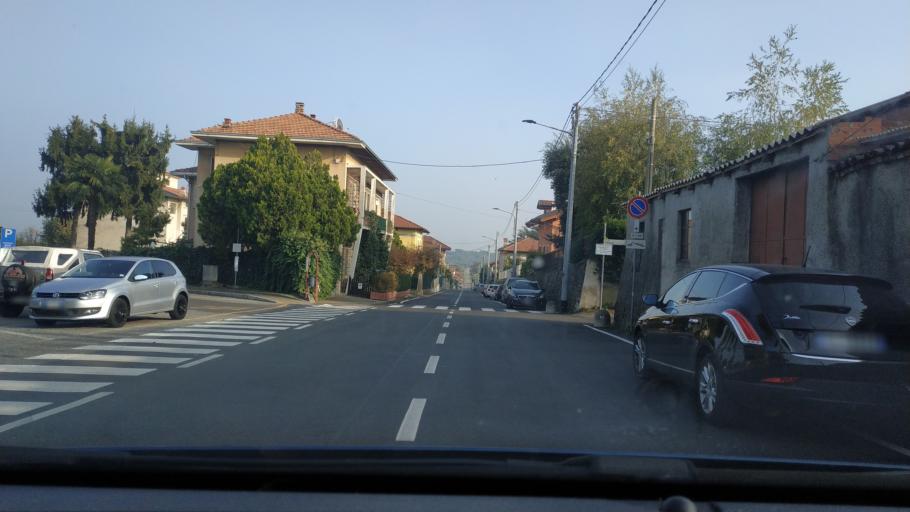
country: IT
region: Piedmont
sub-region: Provincia di Biella
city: Candelo
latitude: 45.5451
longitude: 8.1148
